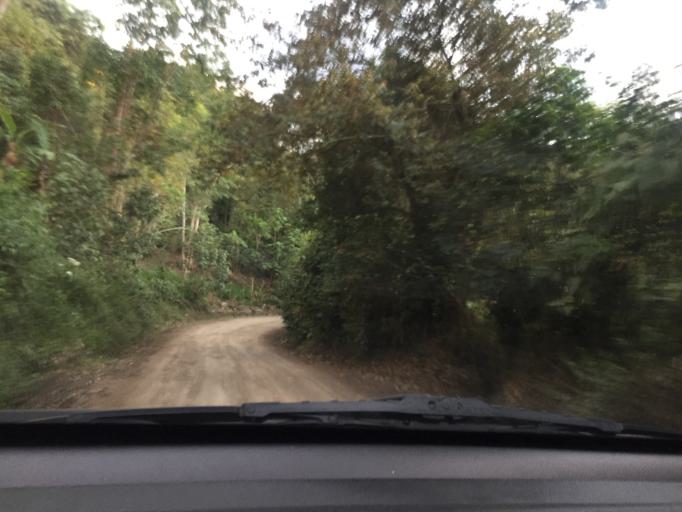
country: CO
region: Cundinamarca
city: Zipacon
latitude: 4.7032
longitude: -74.4088
